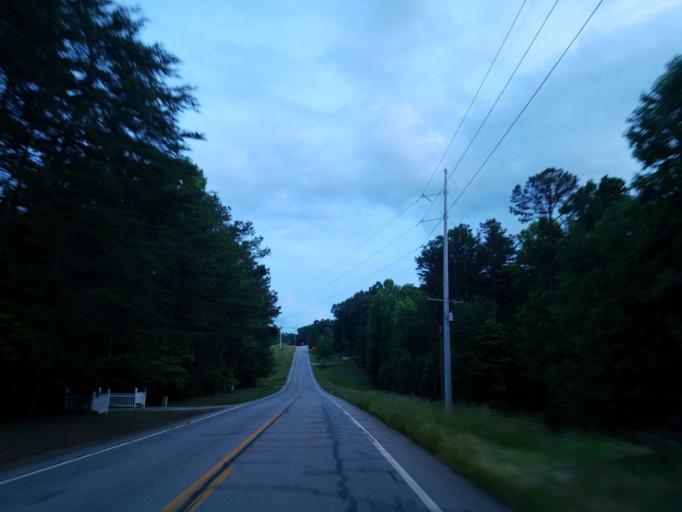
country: US
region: Georgia
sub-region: Dawson County
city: Dawsonville
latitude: 34.4392
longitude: -84.1633
